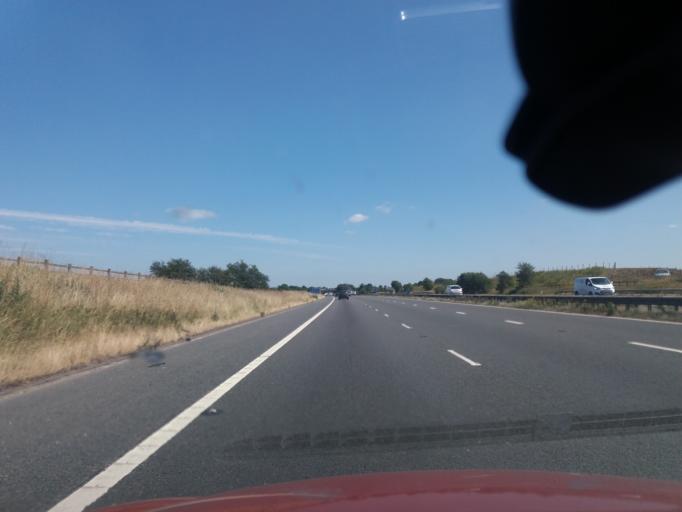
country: GB
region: England
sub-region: Borough of Bolton
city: Westhoughton
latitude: 53.5687
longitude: -2.5334
